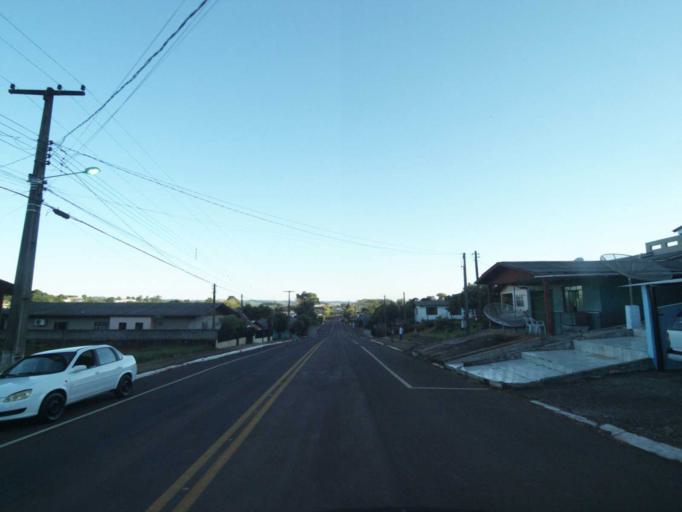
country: BR
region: Parana
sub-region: Coronel Vivida
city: Coronel Vivida
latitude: -25.9560
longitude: -52.8182
